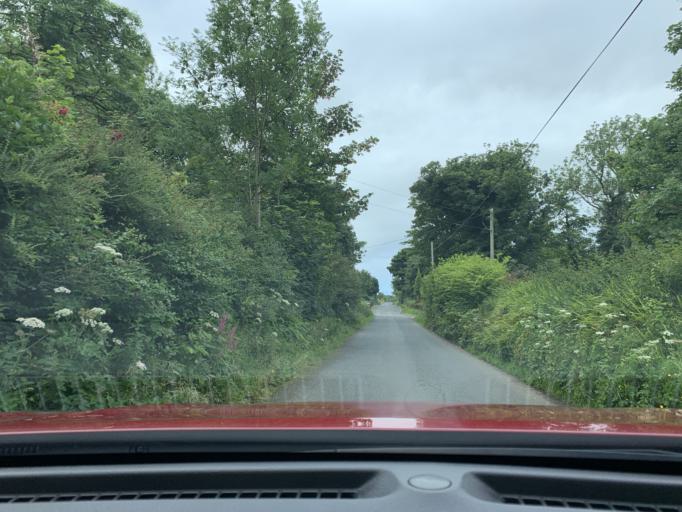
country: IE
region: Connaught
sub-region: County Leitrim
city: Kinlough
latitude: 54.4000
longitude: -8.4097
